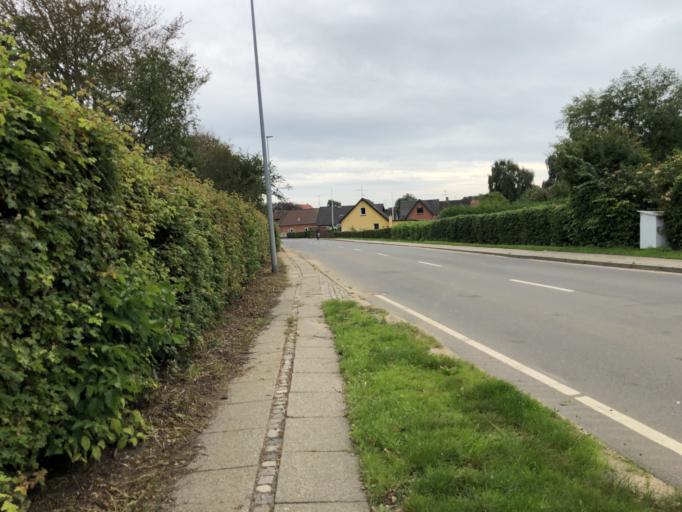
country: DK
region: North Denmark
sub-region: Morso Kommune
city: Nykobing Mors
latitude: 56.7972
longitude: 8.8519
